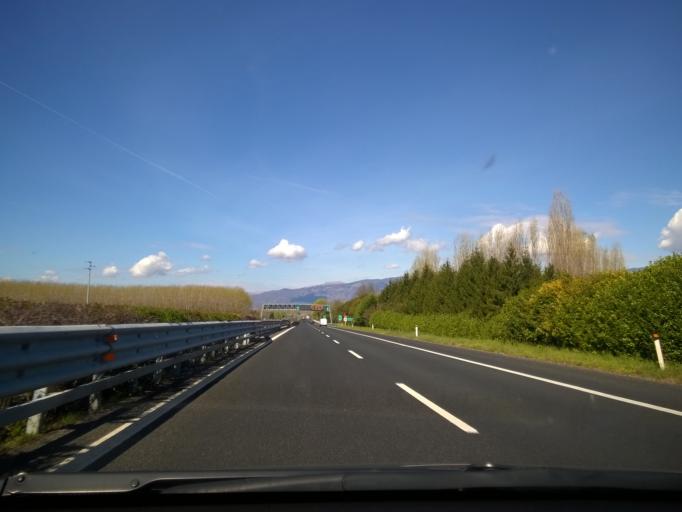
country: IT
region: Friuli Venezia Giulia
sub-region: Provincia di Pordenone
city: Porcia
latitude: 45.9439
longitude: 12.6027
